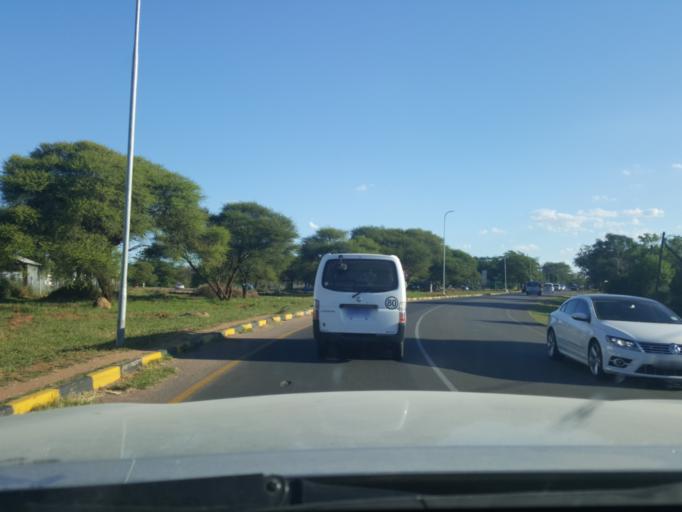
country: BW
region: South East
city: Gaborone
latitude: -24.6408
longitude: 25.9397
